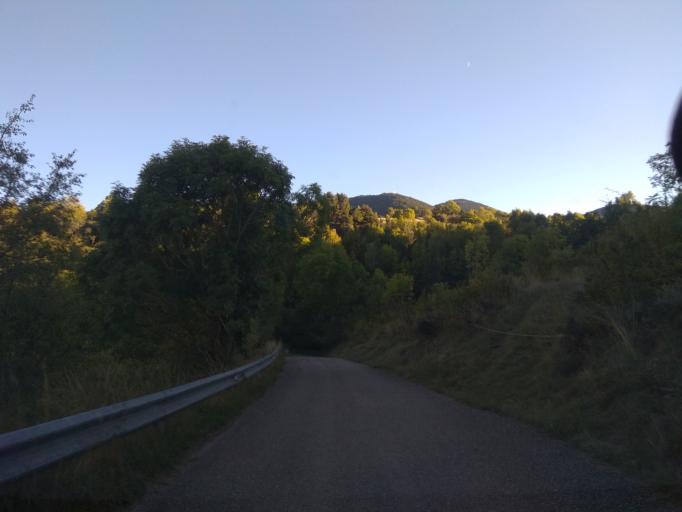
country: ES
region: Catalonia
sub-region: Provincia de Lleida
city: Lles de Cerdanya
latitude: 42.3541
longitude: 1.7157
